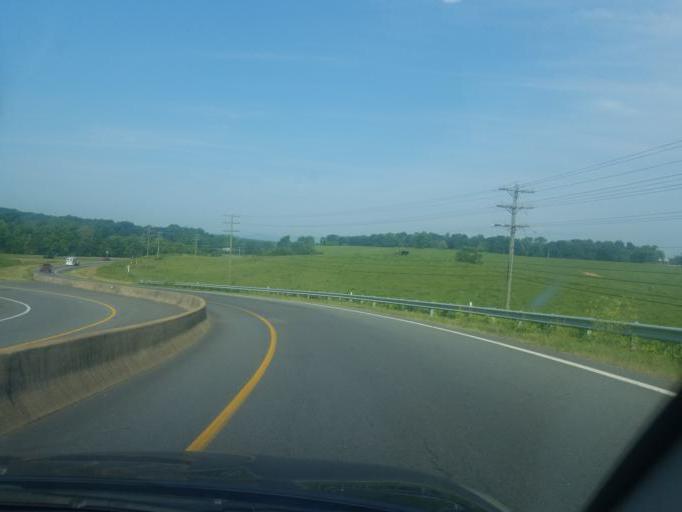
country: US
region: Virginia
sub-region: Culpeper County
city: Culpeper
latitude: 38.4554
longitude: -78.0233
